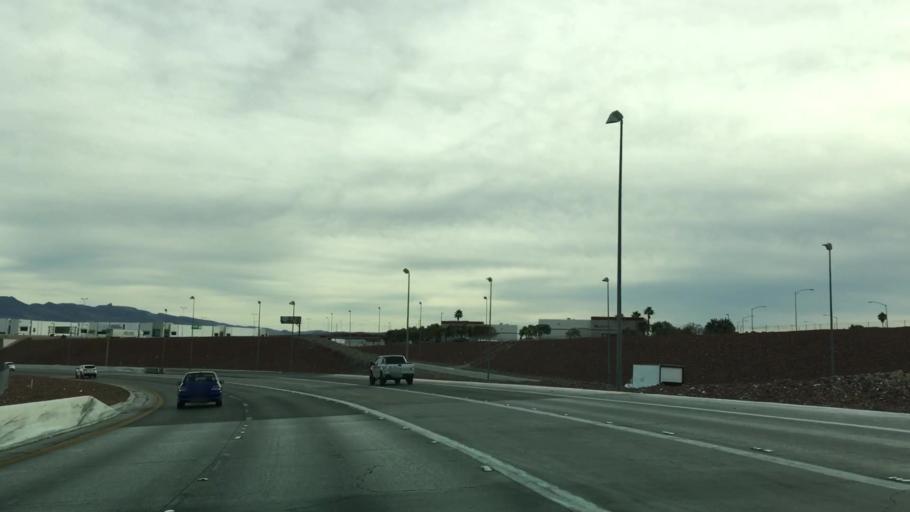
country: US
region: Nevada
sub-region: Clark County
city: Paradise
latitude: 36.0630
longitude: -115.1833
